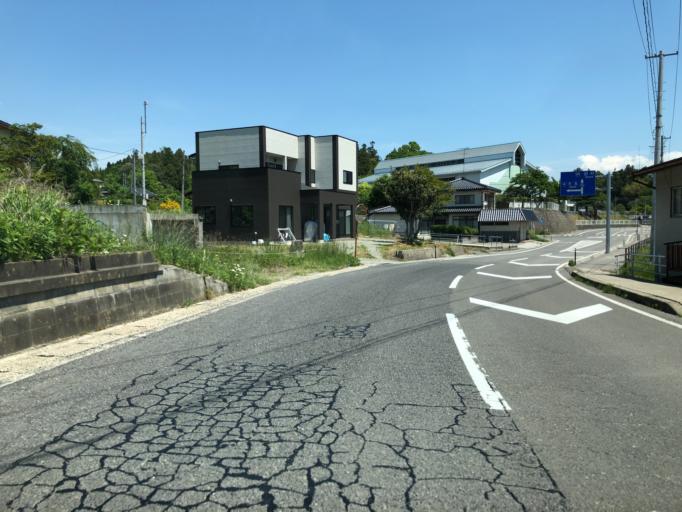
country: JP
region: Fukushima
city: Miharu
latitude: 37.5014
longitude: 140.4722
